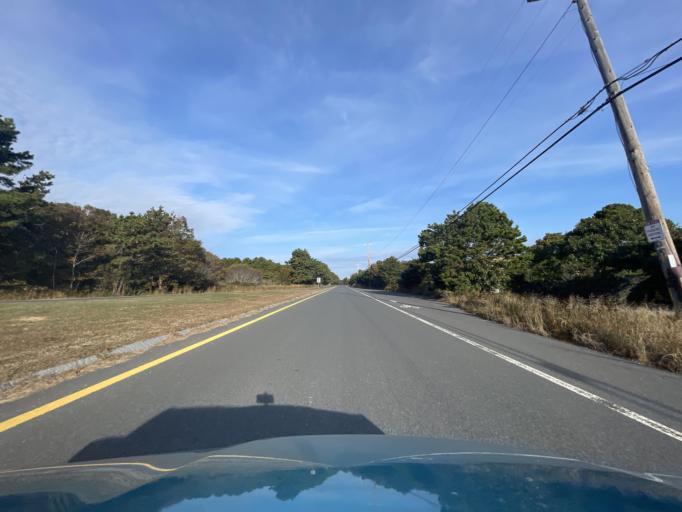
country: US
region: Massachusetts
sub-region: Bristol County
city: Head of Westport
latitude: 41.5005
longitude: -71.0378
